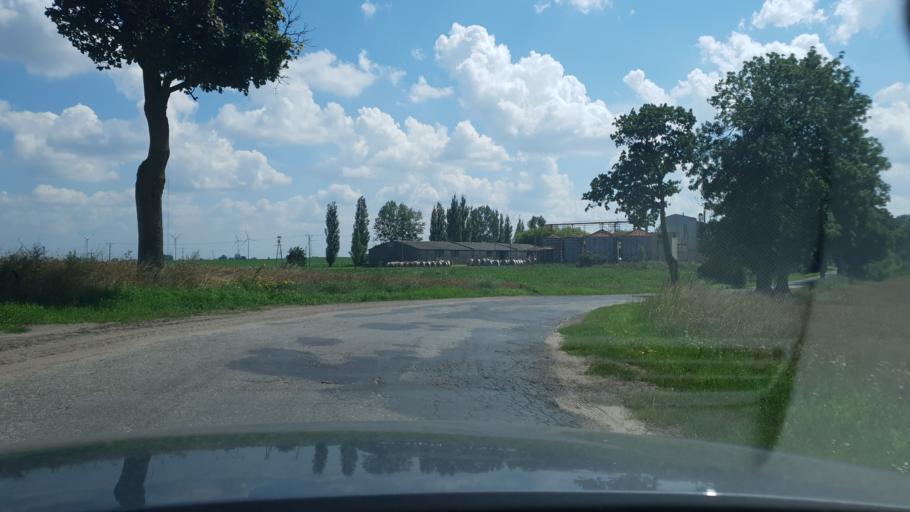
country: PL
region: Kujawsko-Pomorskie
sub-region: Powiat wabrzeski
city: Pluznica
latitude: 53.3513
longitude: 18.8284
